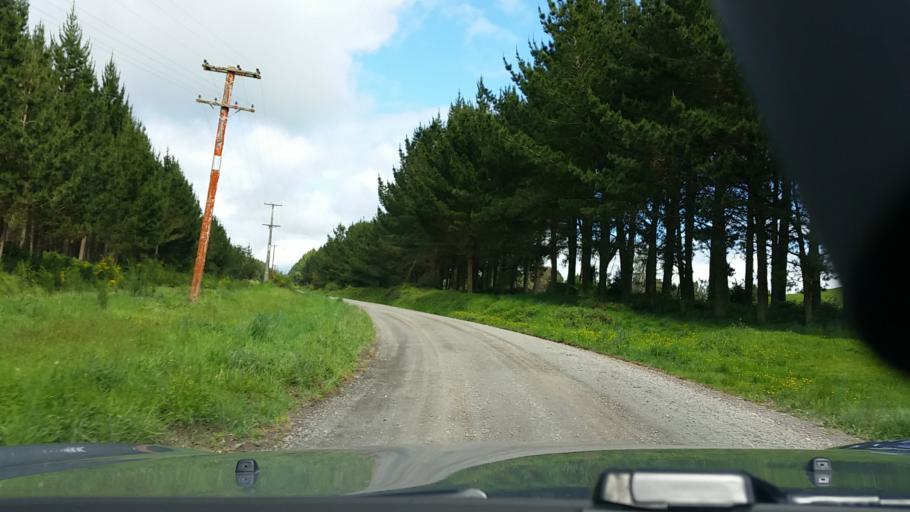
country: NZ
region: Bay of Plenty
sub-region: Whakatane District
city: Murupara
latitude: -38.3488
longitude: 176.4957
